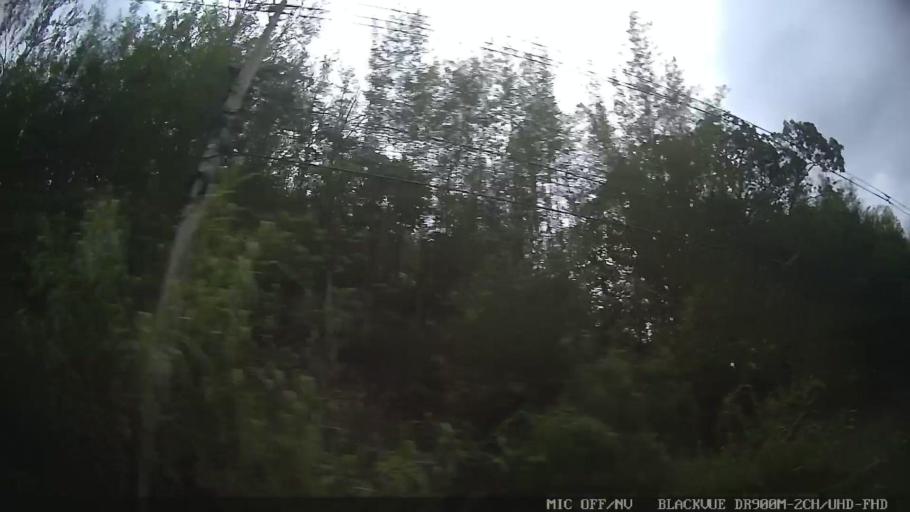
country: BR
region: Sao Paulo
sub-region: Amparo
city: Amparo
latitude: -22.7210
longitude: -46.7704
